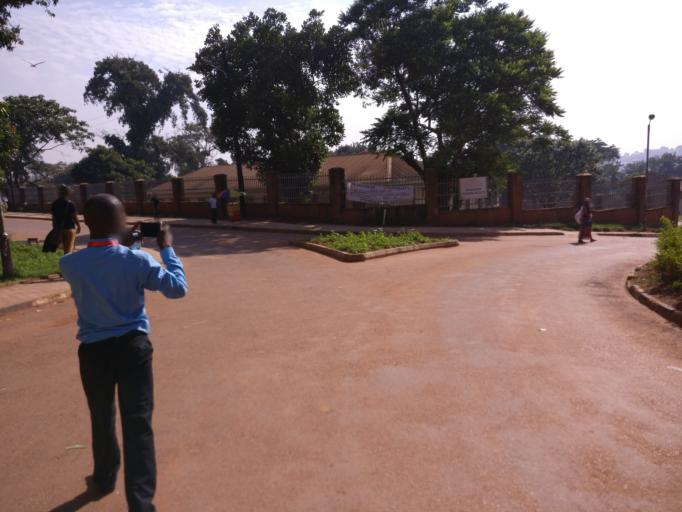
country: UG
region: Central Region
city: Kampala Central Division
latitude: 0.3364
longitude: 32.5683
